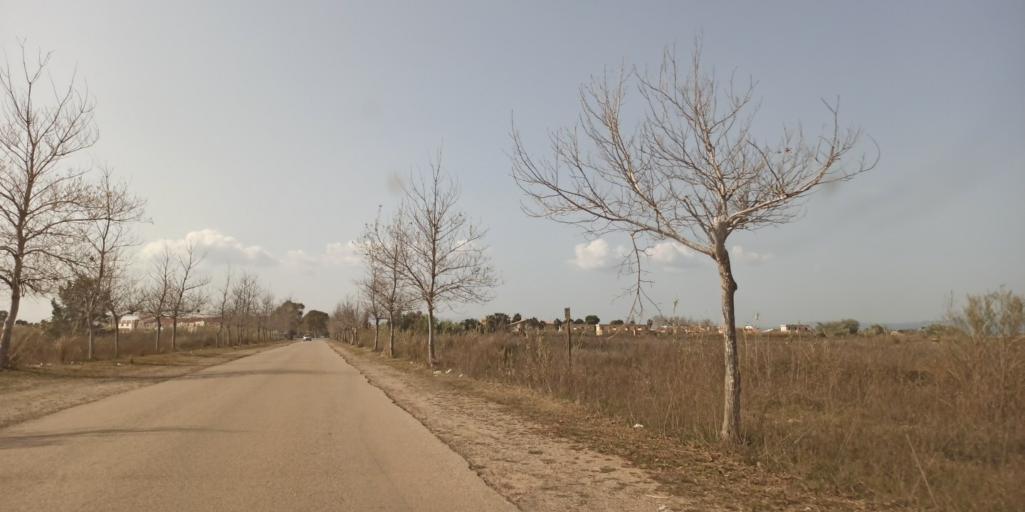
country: ES
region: Catalonia
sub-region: Provincia de Tarragona
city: Deltebre
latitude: 40.7219
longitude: 0.8455
